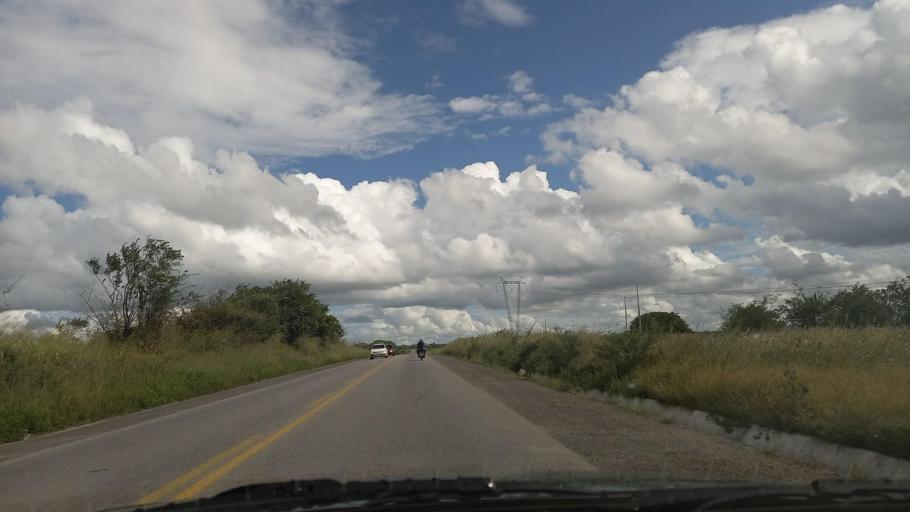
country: BR
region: Pernambuco
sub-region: Lajedo
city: Lajedo
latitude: -8.5973
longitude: -36.2915
